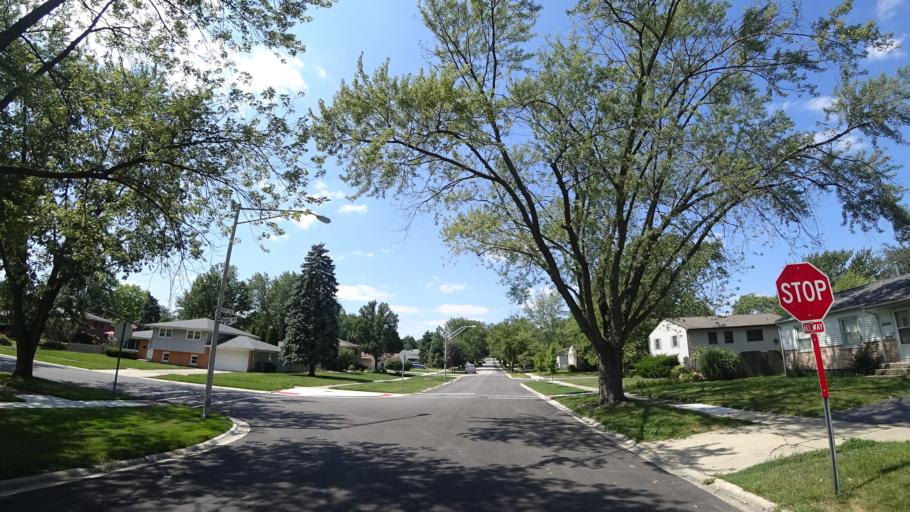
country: US
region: Illinois
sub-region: Cook County
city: Orland Park
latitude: 41.6235
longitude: -87.8373
